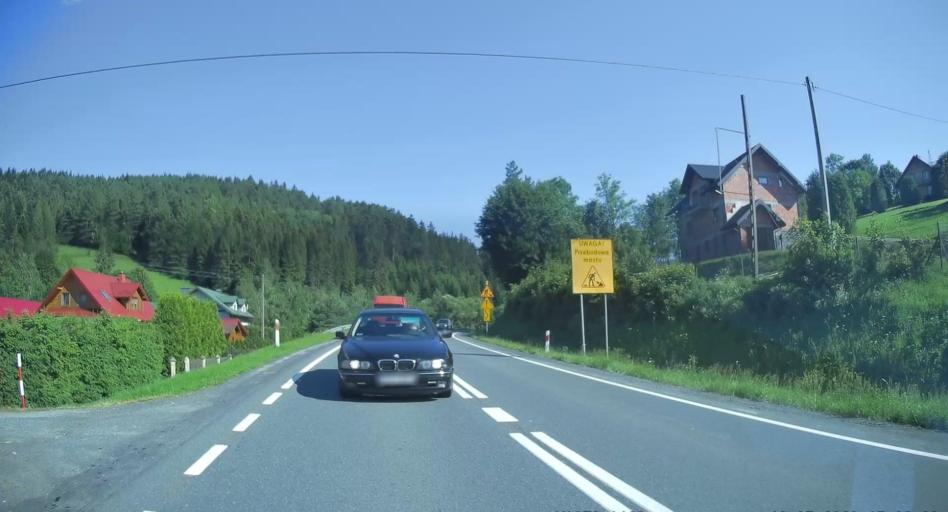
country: PL
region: Lesser Poland Voivodeship
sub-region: Powiat nowosadecki
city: Labowa
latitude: 49.4881
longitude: 20.9141
